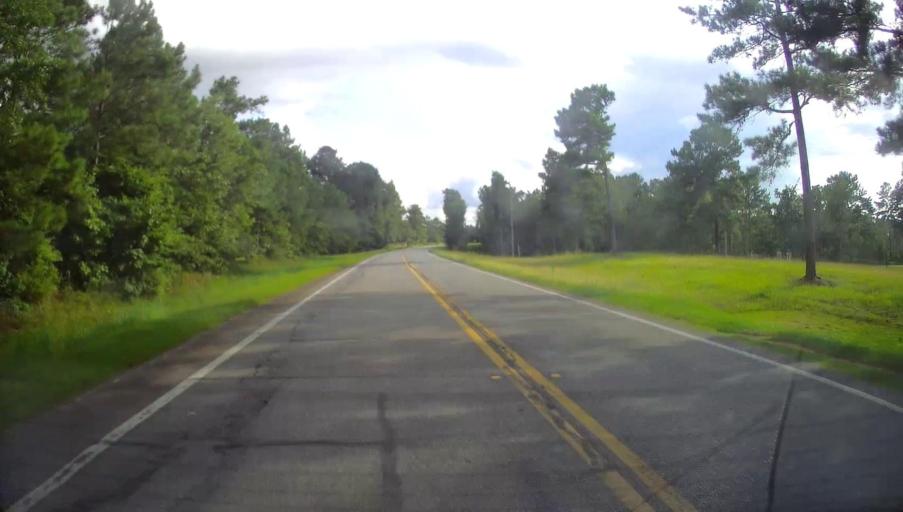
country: US
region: Georgia
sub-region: Crawford County
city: Roberta
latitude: 32.8146
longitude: -84.0244
